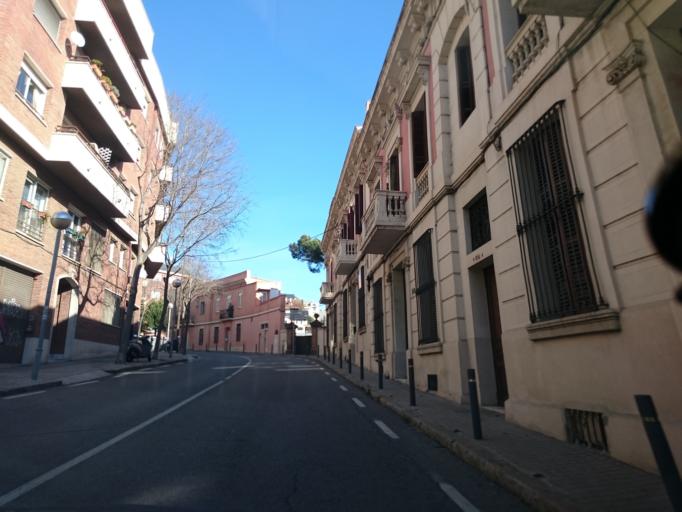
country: ES
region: Catalonia
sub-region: Provincia de Barcelona
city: les Corts
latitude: 41.4116
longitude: 2.1039
